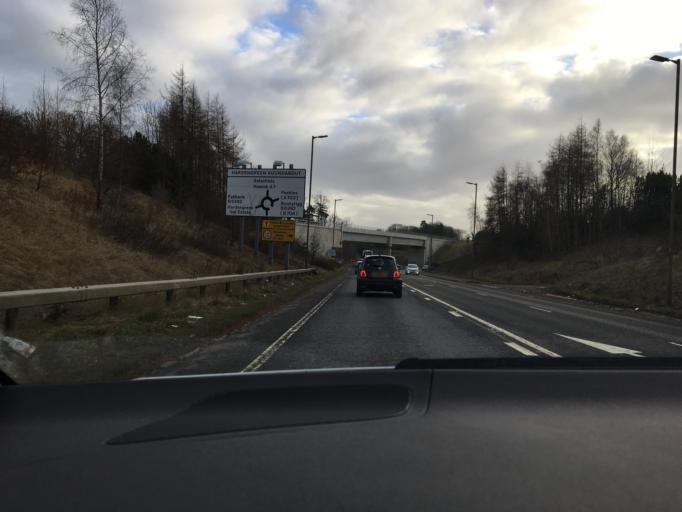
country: GB
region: Scotland
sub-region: Midlothian
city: Bonnyrigg
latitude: 55.8779
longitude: -3.0842
